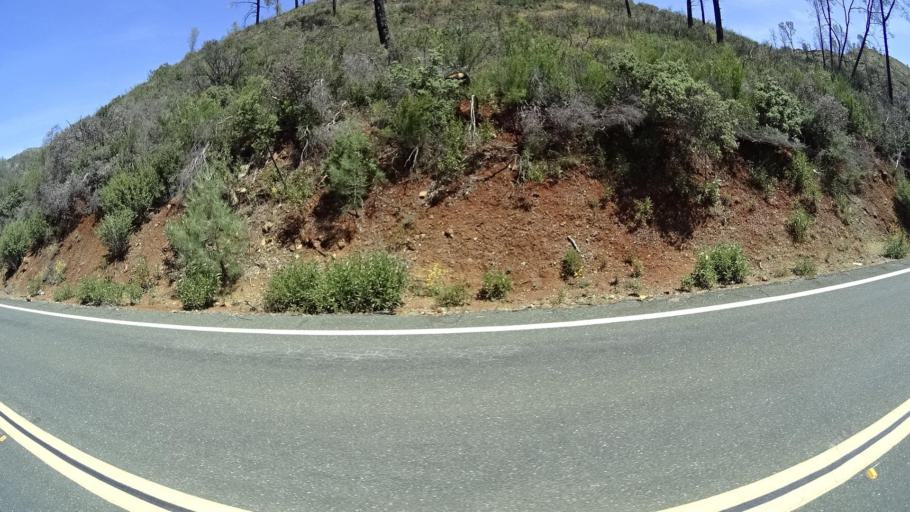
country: US
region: California
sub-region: Lake County
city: Hidden Valley Lake
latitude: 38.7169
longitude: -122.4902
